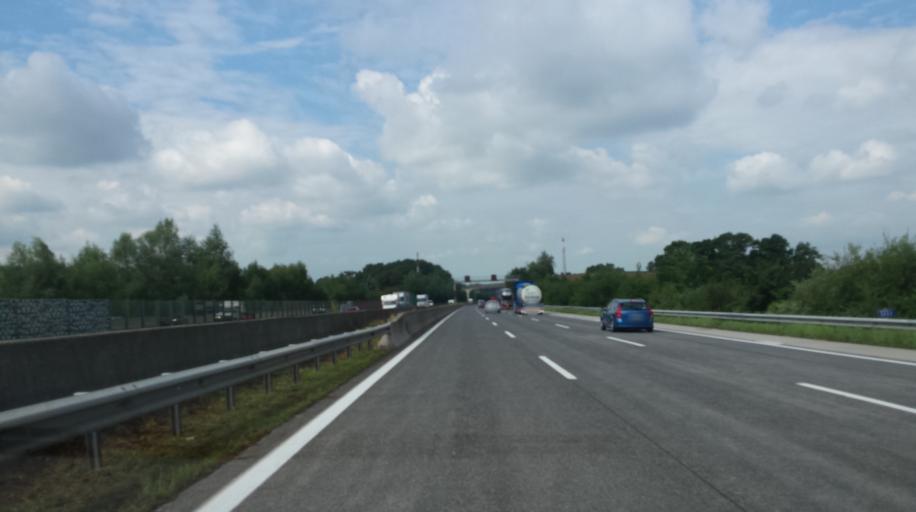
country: AT
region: Lower Austria
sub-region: Politischer Bezirk Amstetten
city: Wolfsbach
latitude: 48.1142
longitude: 14.7004
